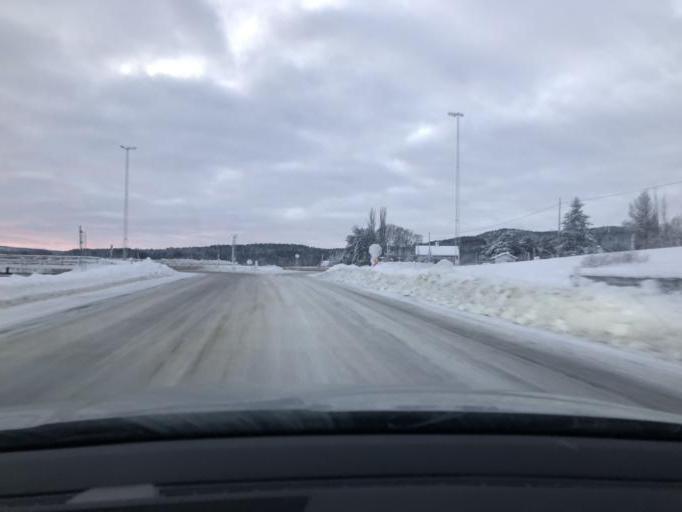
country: SE
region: Vaesternorrland
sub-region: Kramfors Kommun
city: Nordingra
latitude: 62.9272
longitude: 18.0995
